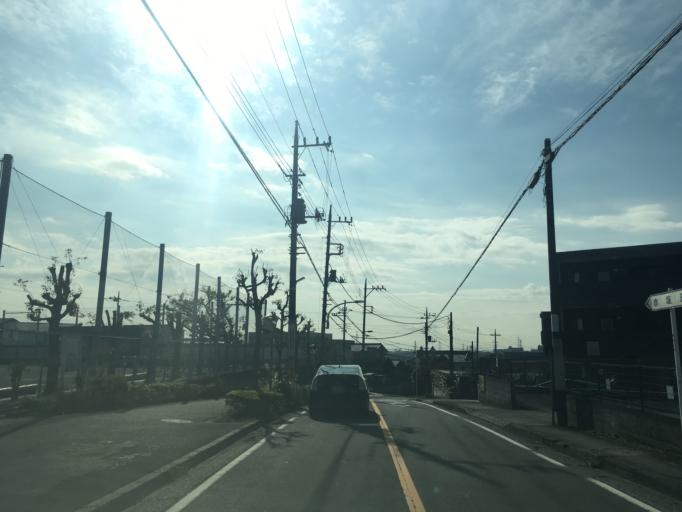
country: JP
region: Tokyo
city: Higashimurayama-shi
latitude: 35.7588
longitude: 139.4448
